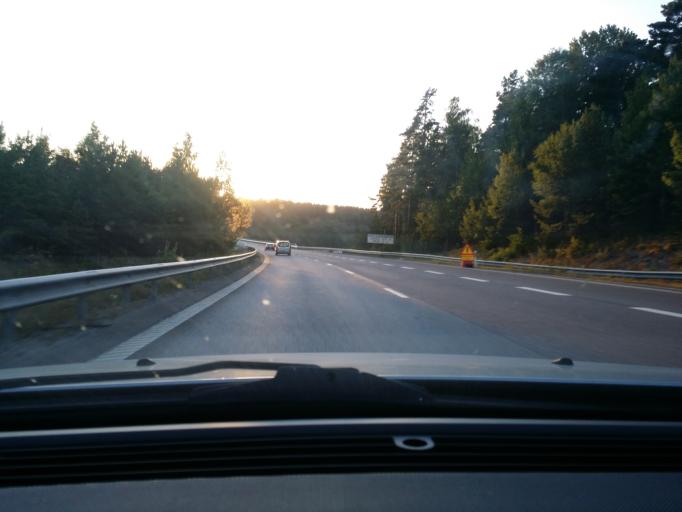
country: SE
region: Uppsala
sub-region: Enkopings Kommun
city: Dalby
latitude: 59.6243
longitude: 17.3902
